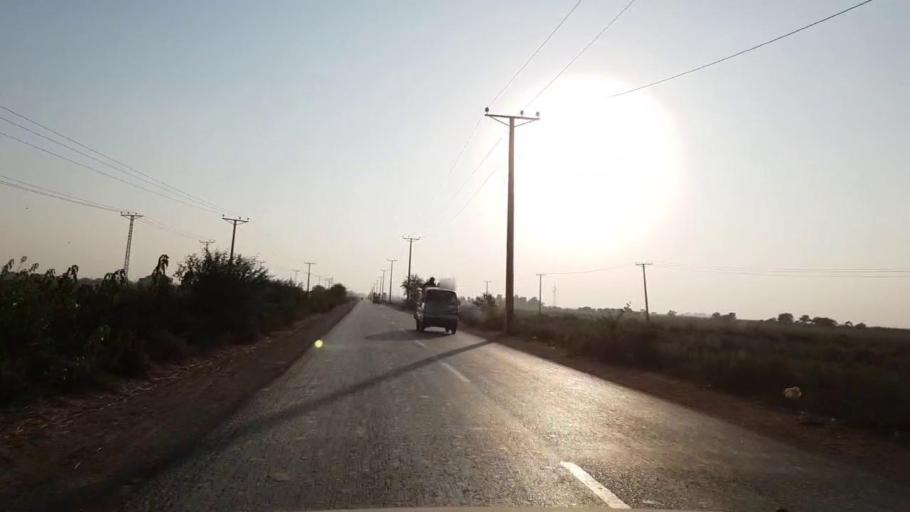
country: PK
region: Sindh
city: Daro Mehar
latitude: 24.6225
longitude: 68.0970
